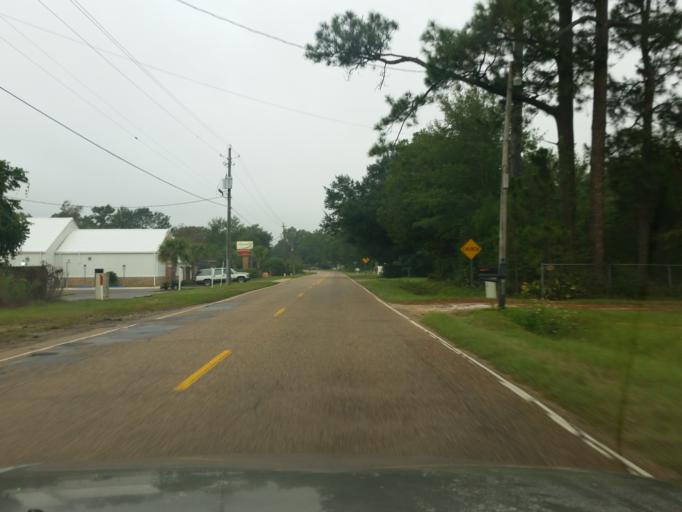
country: US
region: Florida
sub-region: Escambia County
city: Cantonment
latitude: 30.6069
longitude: -87.3513
